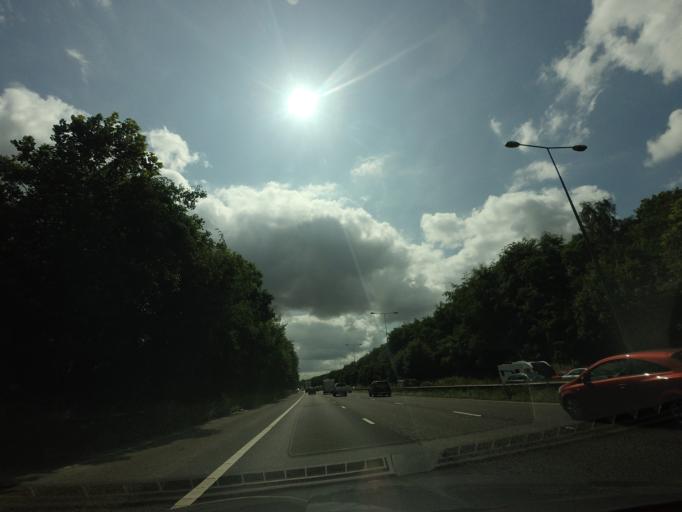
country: GB
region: England
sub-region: St. Helens
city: Billinge
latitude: 53.5249
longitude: -2.6975
